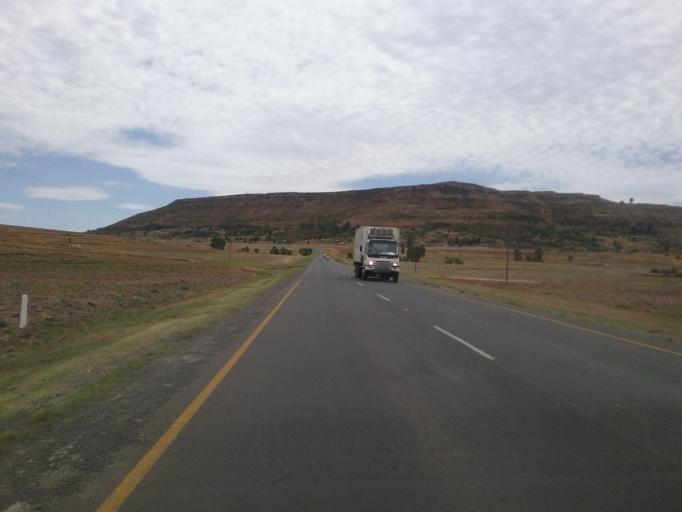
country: LS
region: Maseru
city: Nako
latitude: -29.6154
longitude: 27.4993
